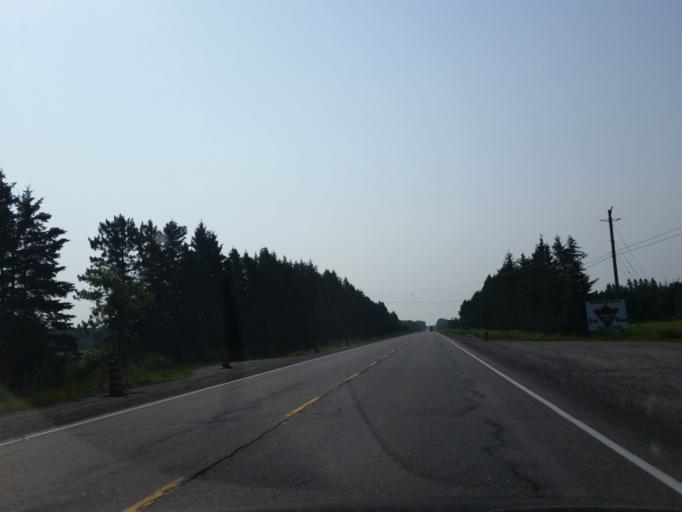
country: CA
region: Ontario
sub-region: Nipissing District
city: North Bay
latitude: 46.3925
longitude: -80.0057
